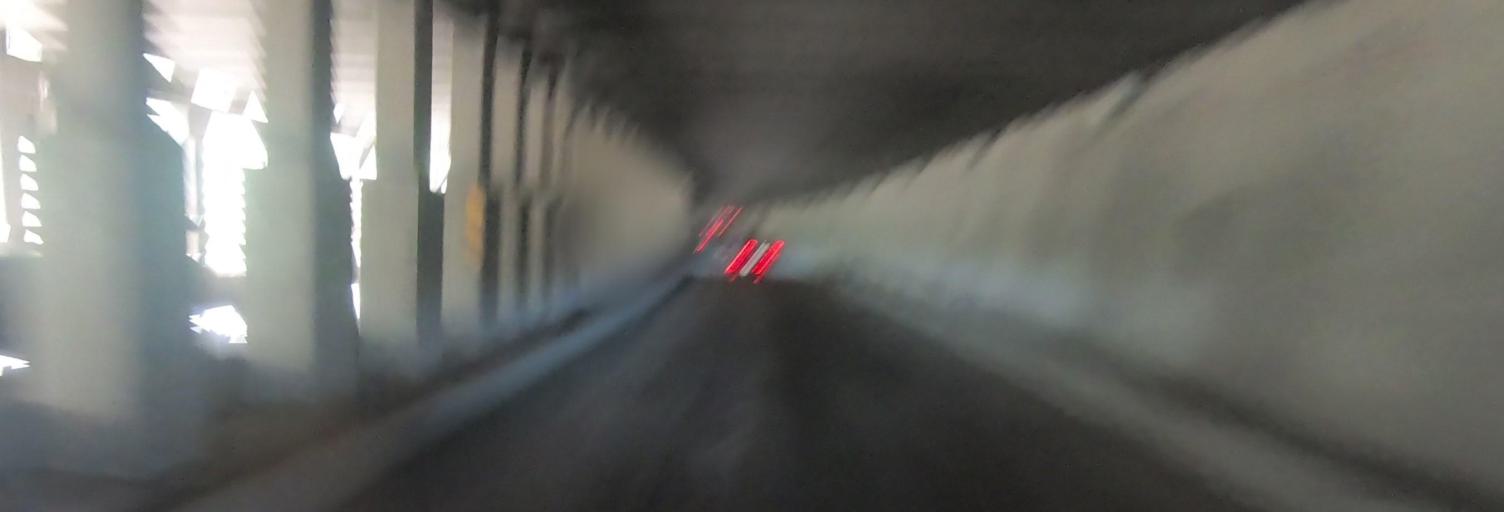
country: CA
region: British Columbia
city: Golden
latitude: 51.3284
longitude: -117.4602
